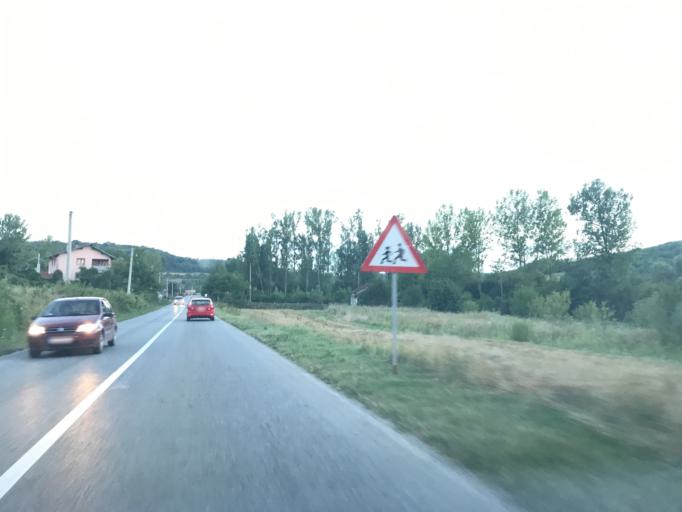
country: RS
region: Central Serbia
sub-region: Branicevski Okrug
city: Veliko Gradiste
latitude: 44.7153
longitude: 21.3965
